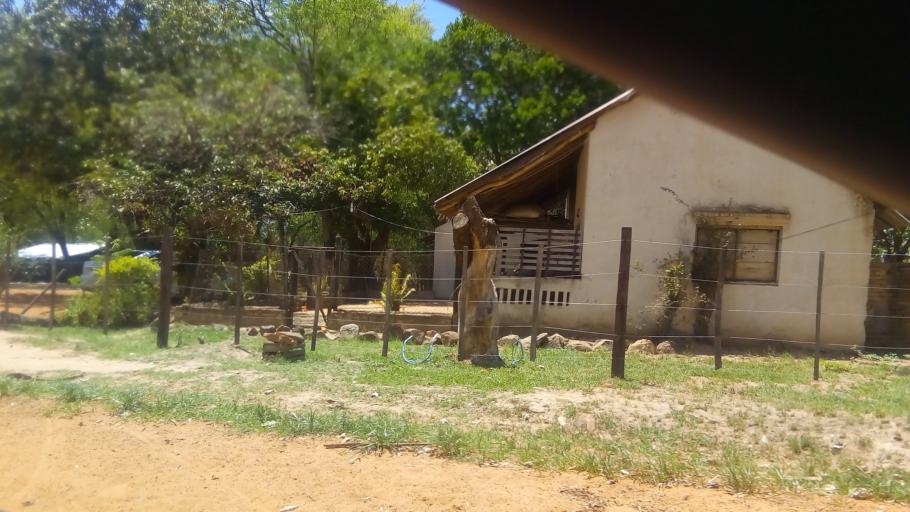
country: PY
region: Cordillera
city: Arroyos y Esteros
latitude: -24.9939
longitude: -57.2147
